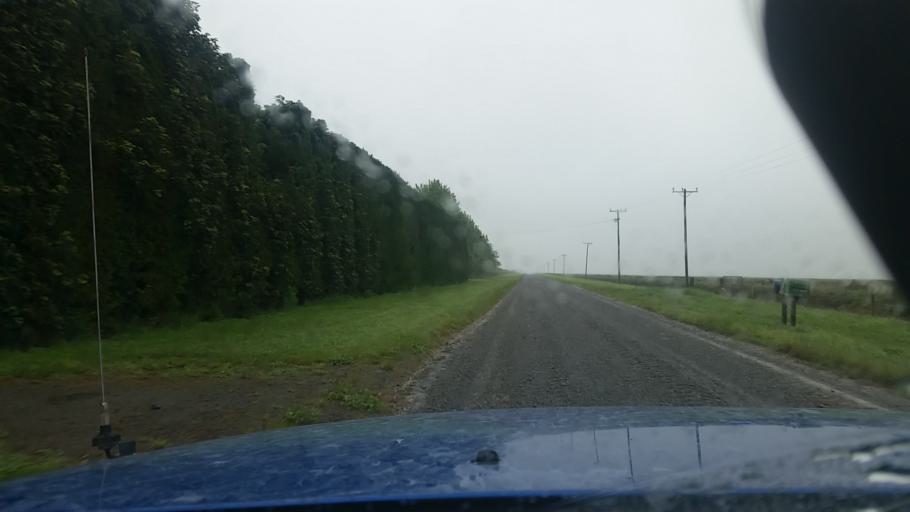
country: NZ
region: Canterbury
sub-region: Ashburton District
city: Rakaia
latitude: -43.7127
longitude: 171.8999
